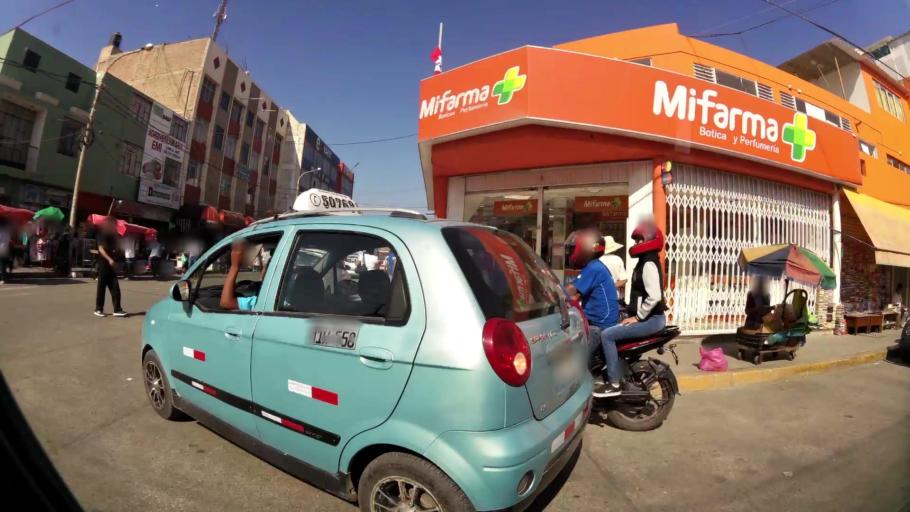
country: PE
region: Lambayeque
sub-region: Provincia de Chiclayo
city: Chiclayo
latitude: -6.7665
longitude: -79.8411
